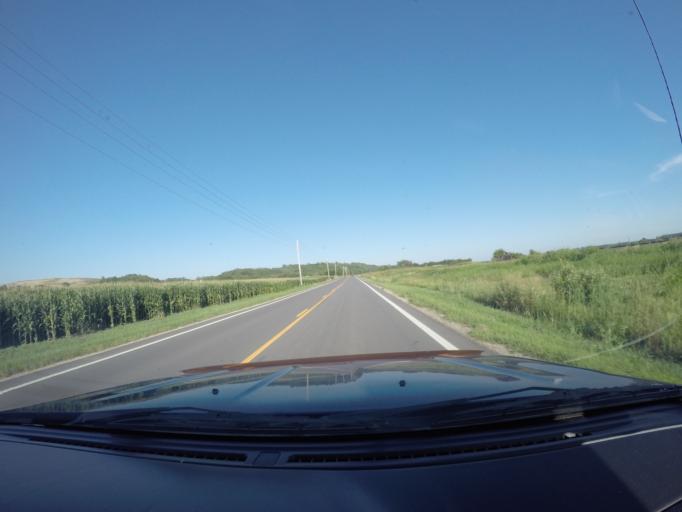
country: US
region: Kansas
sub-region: Douglas County
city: Lawrence
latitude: 39.0514
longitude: -95.2844
